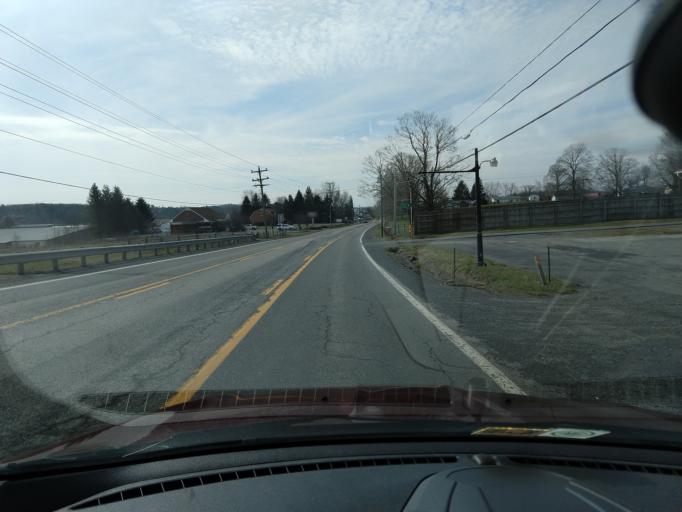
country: US
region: West Virginia
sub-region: Greenbrier County
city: Lewisburg
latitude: 37.8388
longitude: -80.4157
